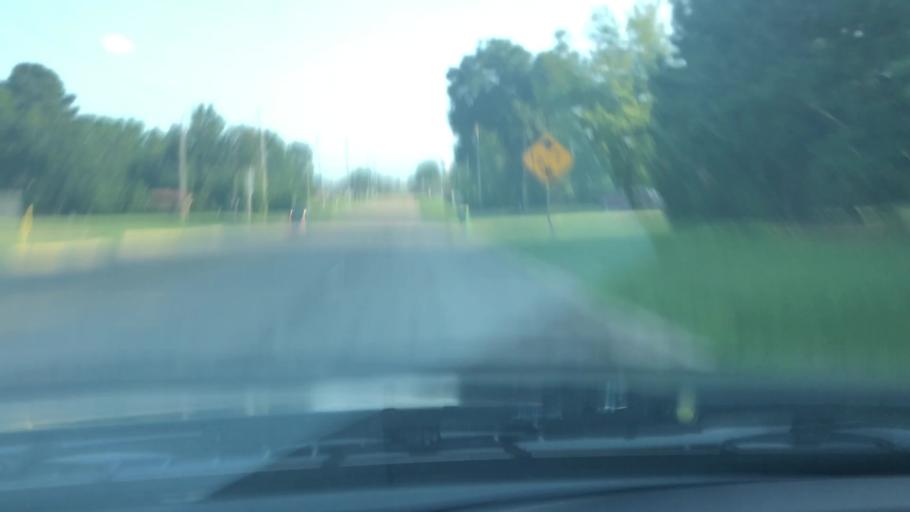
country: US
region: Texas
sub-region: Bowie County
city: Wake Village
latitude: 33.3899
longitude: -94.0923
